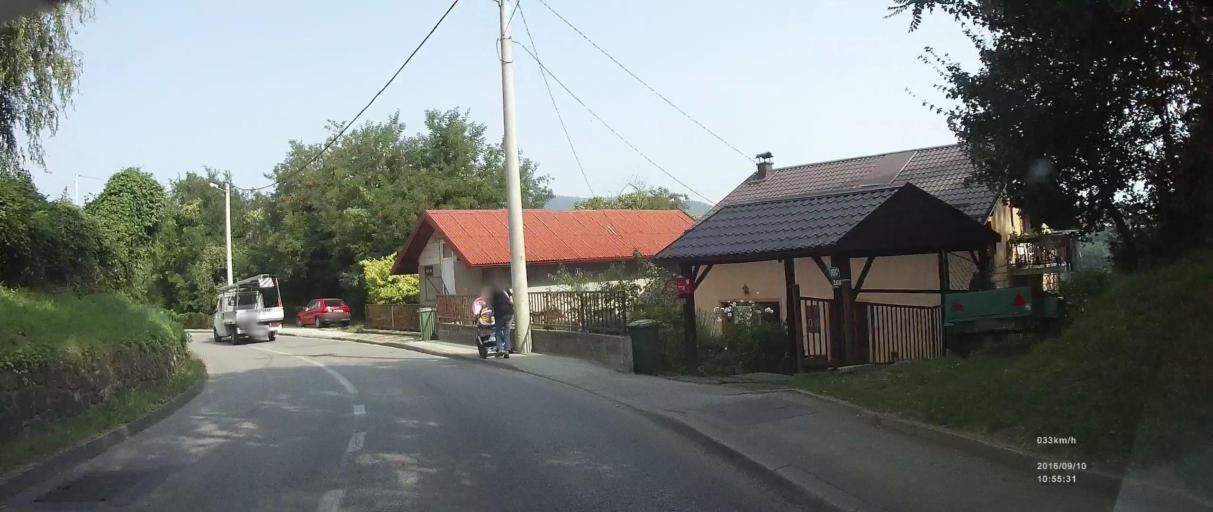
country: HR
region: Grad Zagreb
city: Zagreb
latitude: 45.8316
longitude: 15.9396
